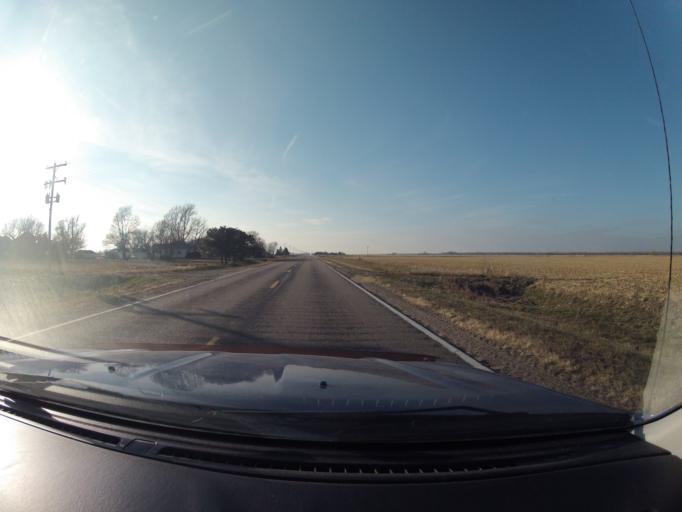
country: US
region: Nebraska
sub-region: Buffalo County
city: Kearney
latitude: 40.6410
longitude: -99.0417
